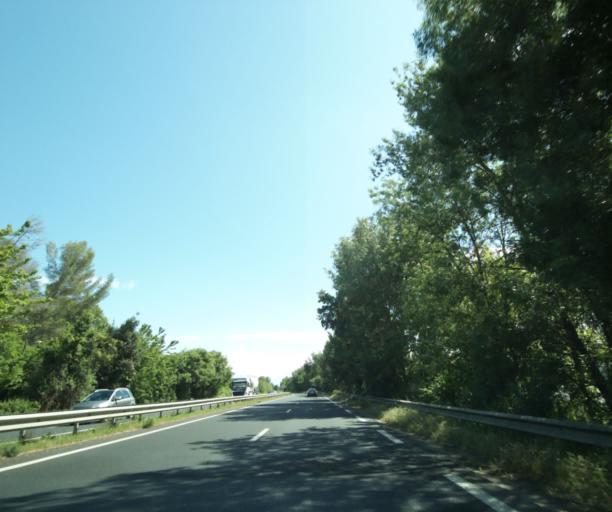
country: FR
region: Languedoc-Roussillon
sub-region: Departement de l'Herault
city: Juvignac
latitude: 43.6035
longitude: 3.8196
